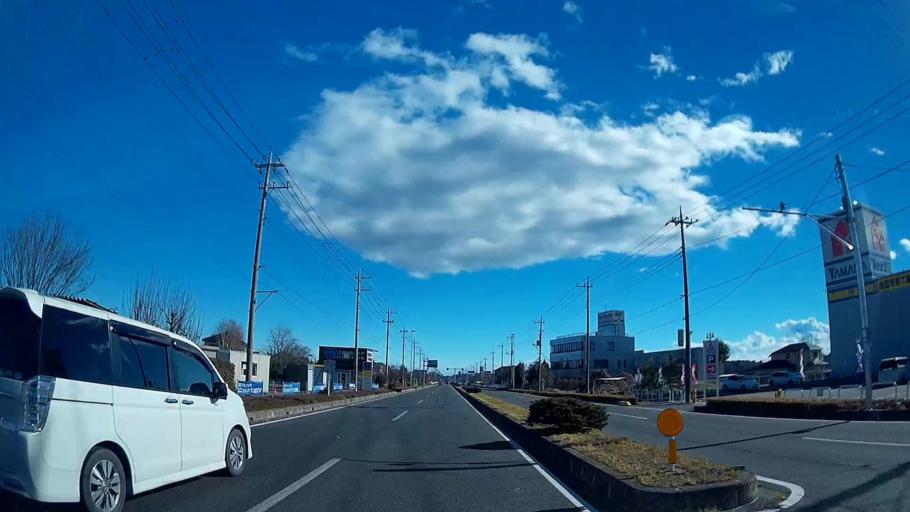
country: JP
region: Saitama
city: Yorii
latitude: 36.1219
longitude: 139.2178
